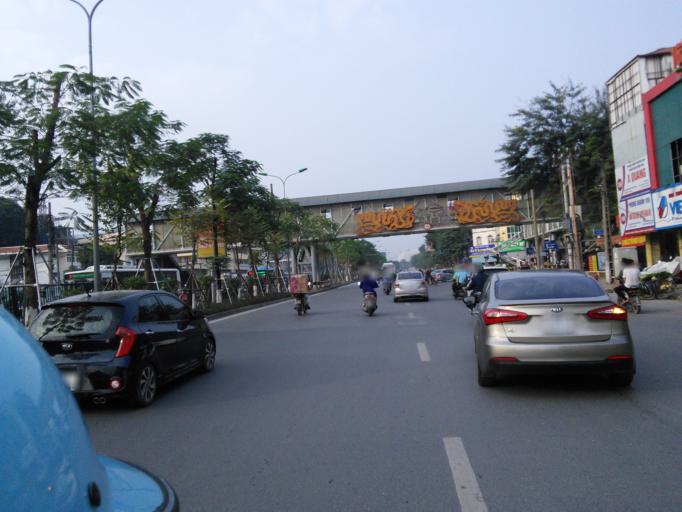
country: VN
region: Ha Noi
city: Hai BaTrung
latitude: 21.0012
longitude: 105.8414
